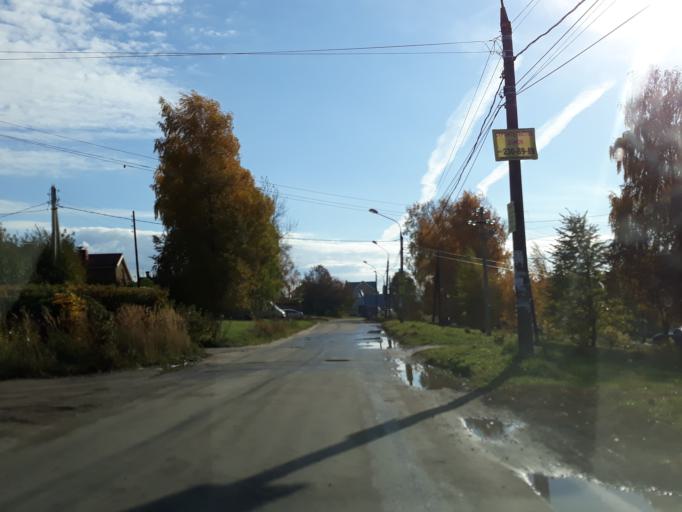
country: RU
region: Nizjnij Novgorod
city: Afonino
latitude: 56.2327
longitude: 44.0065
